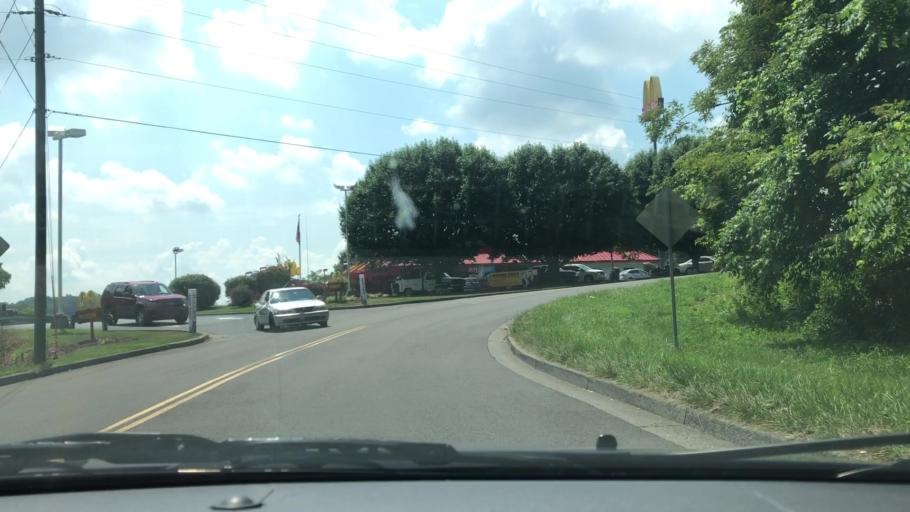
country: US
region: Tennessee
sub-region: Sullivan County
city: Blountville
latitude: 36.5348
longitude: -82.3901
